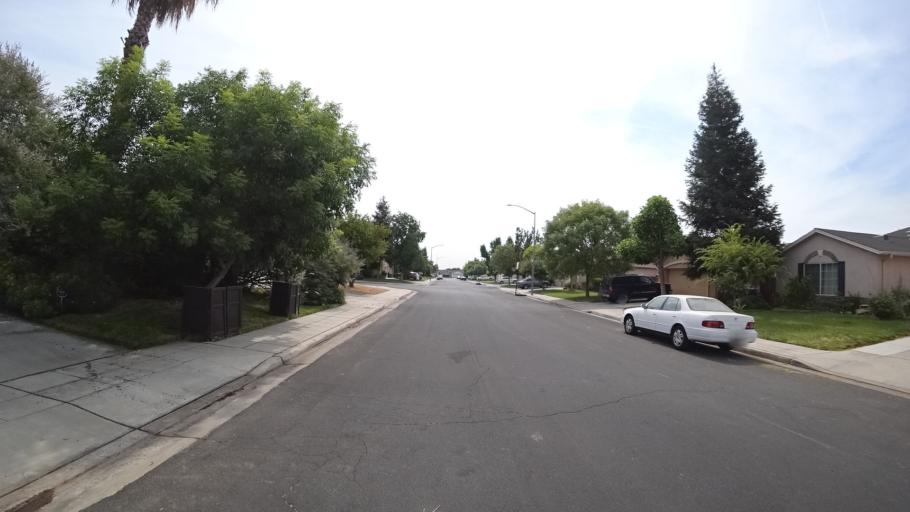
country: US
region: California
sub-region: Fresno County
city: West Park
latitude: 36.7619
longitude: -119.8930
